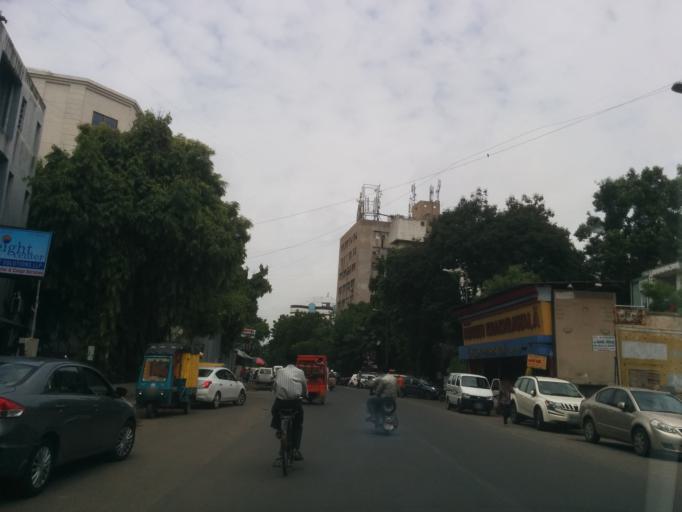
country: IN
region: Gujarat
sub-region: Ahmadabad
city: Ahmedabad
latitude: 23.0324
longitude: 72.5617
